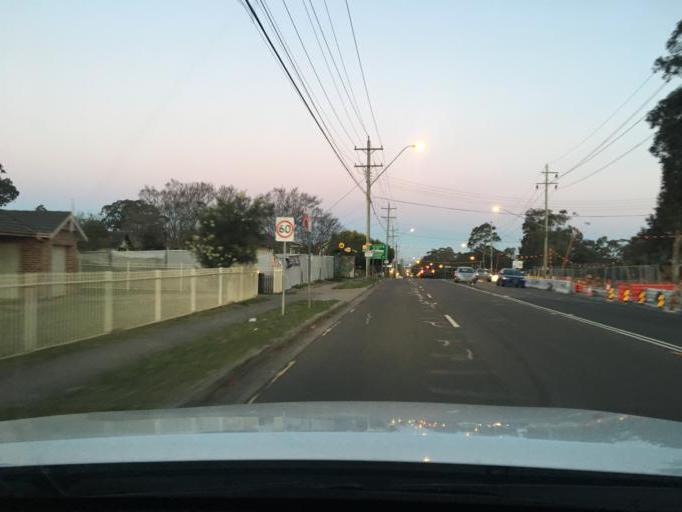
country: AU
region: New South Wales
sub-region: Holroyd
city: Merrylands
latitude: -33.8298
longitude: 150.9582
